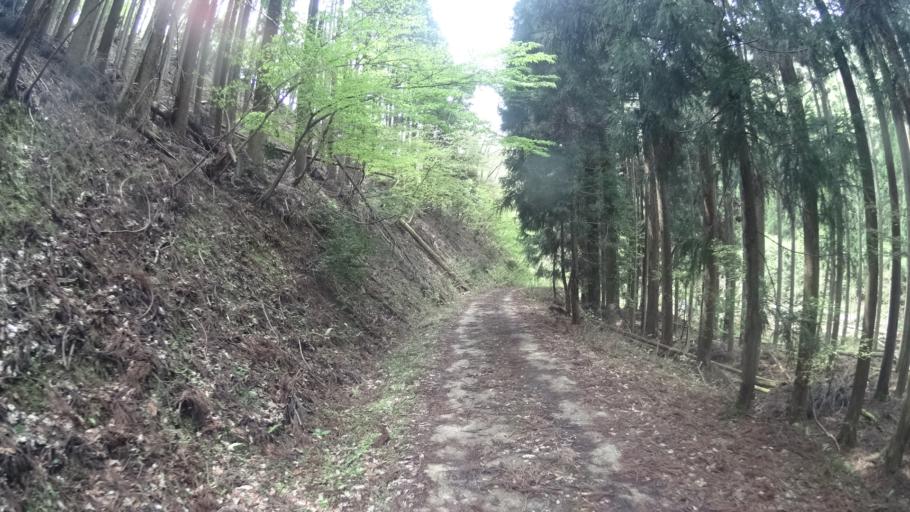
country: JP
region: Kyoto
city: Maizuru
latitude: 35.4044
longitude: 135.5144
